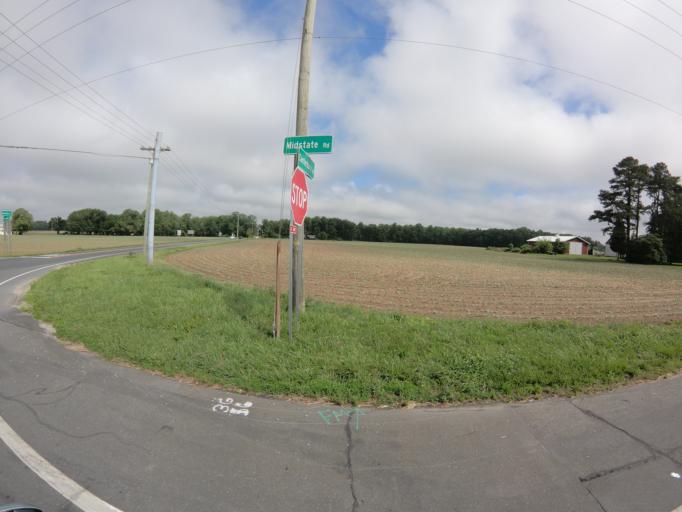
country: US
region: Delaware
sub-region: Kent County
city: Riverview
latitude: 39.0070
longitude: -75.5252
